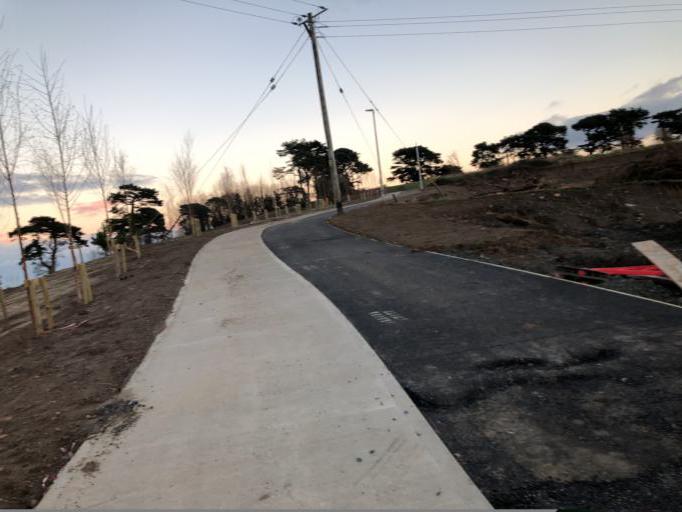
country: IE
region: Leinster
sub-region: Wicklow
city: Greystones
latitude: 53.1406
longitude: -6.0833
